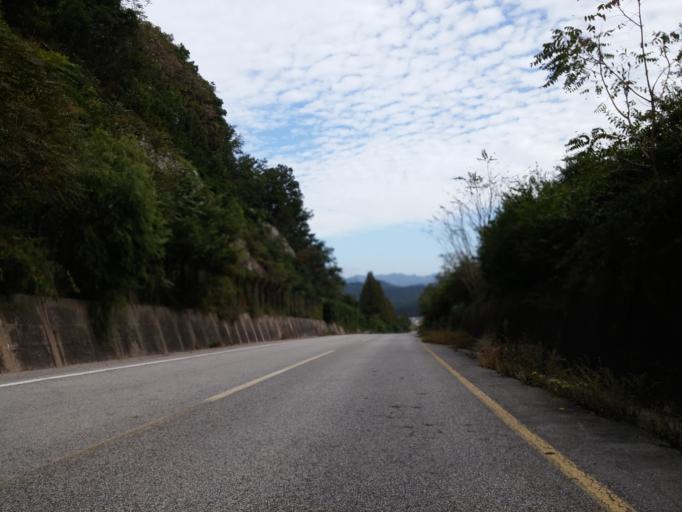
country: KR
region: Chungcheongnam-do
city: Yonmu
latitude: 36.1639
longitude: 127.1946
